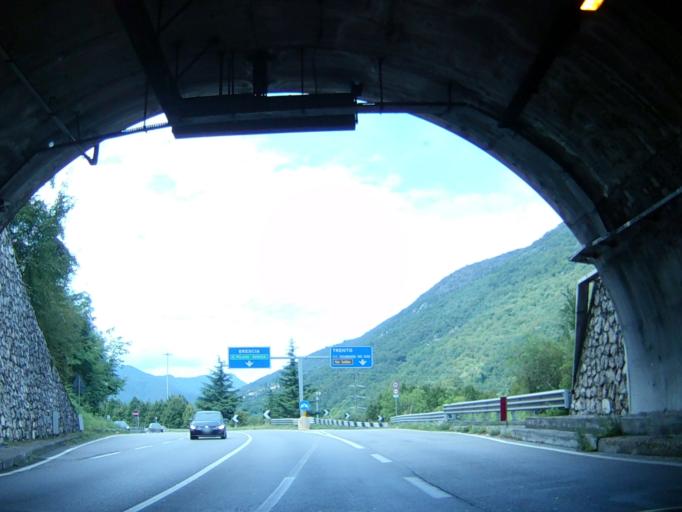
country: IT
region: Lombardy
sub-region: Provincia di Brescia
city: San Giacomo
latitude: 45.6053
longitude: 10.4682
